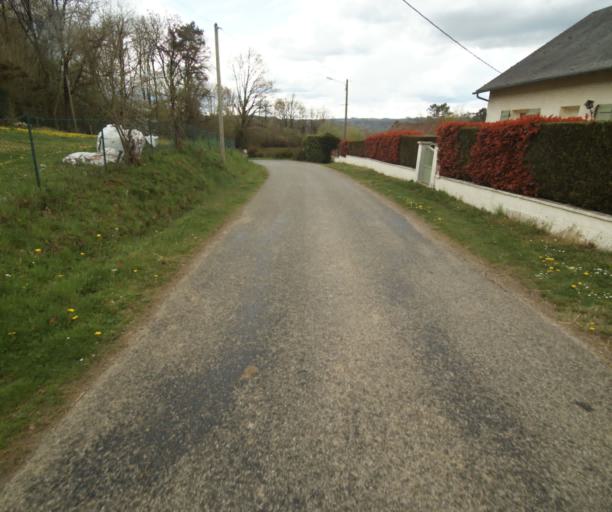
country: FR
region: Limousin
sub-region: Departement de la Correze
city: Laguenne
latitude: 45.2497
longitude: 1.8580
